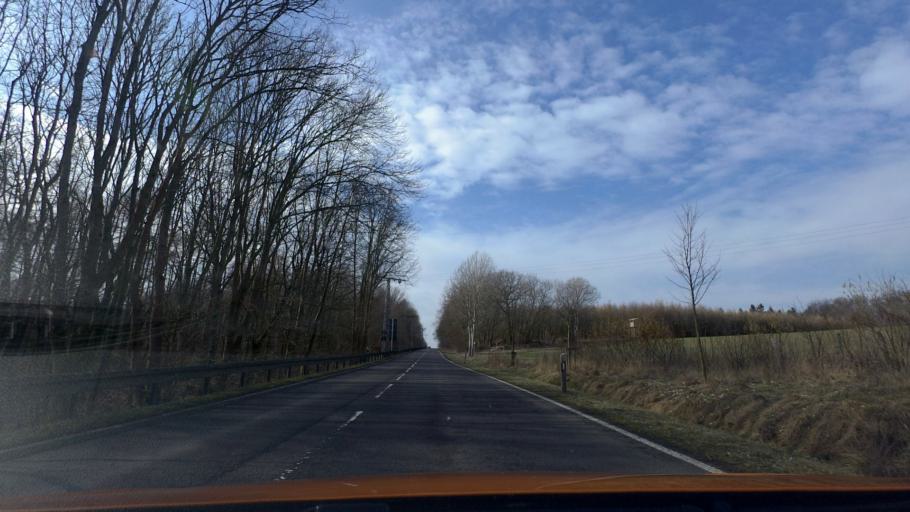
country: DE
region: Saxony-Anhalt
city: Beendorf
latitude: 52.2204
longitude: 11.0996
